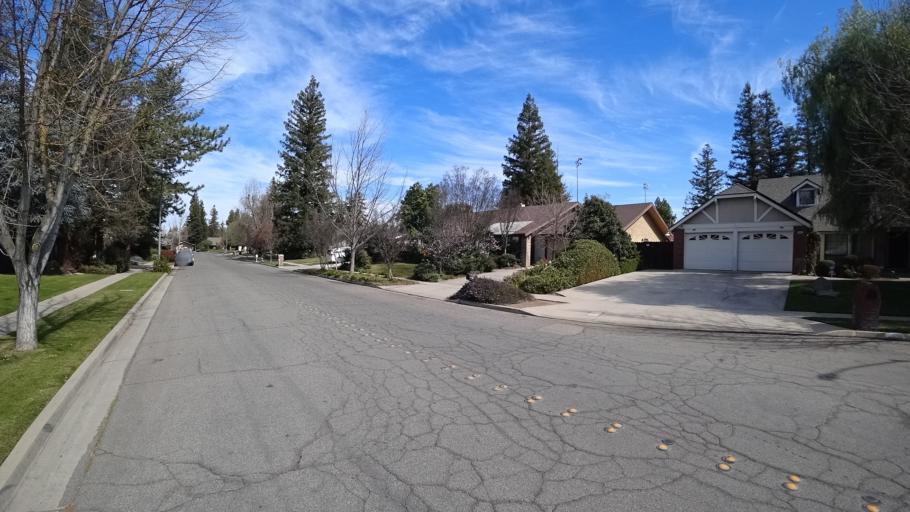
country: US
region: California
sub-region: Fresno County
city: Clovis
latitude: 36.8616
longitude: -119.7687
